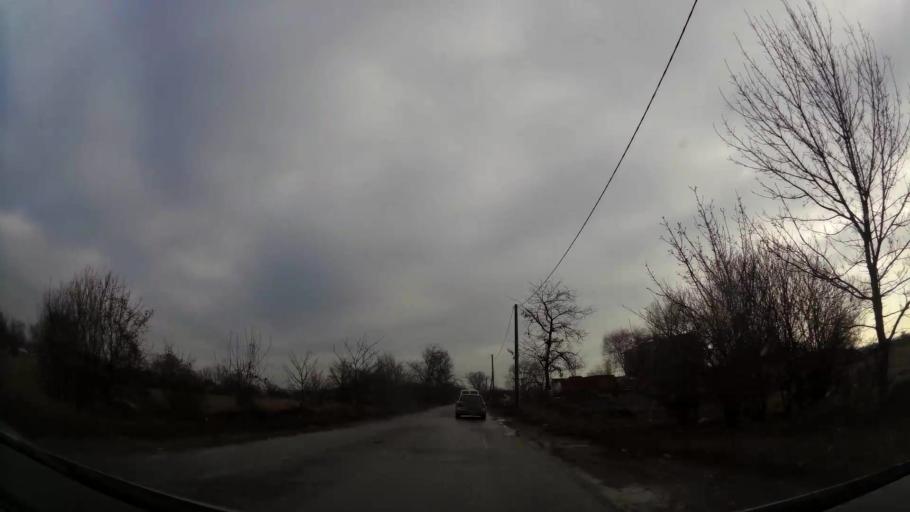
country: BG
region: Sofia-Capital
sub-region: Stolichna Obshtina
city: Sofia
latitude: 42.7243
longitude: 23.3713
